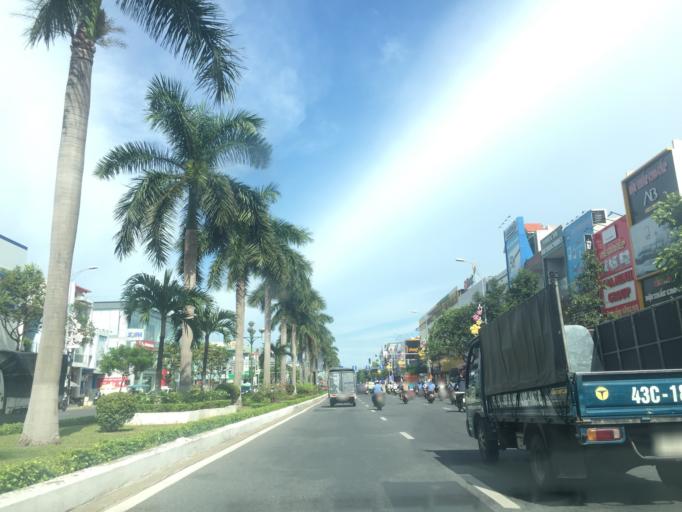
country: VN
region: Da Nang
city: Thanh Khe
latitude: 16.0659
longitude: 108.1907
